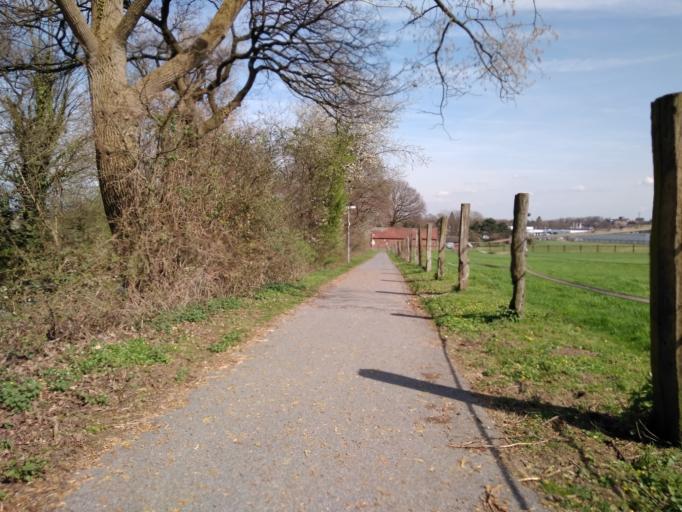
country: DE
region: North Rhine-Westphalia
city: Dorsten
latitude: 51.6551
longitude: 6.9423
